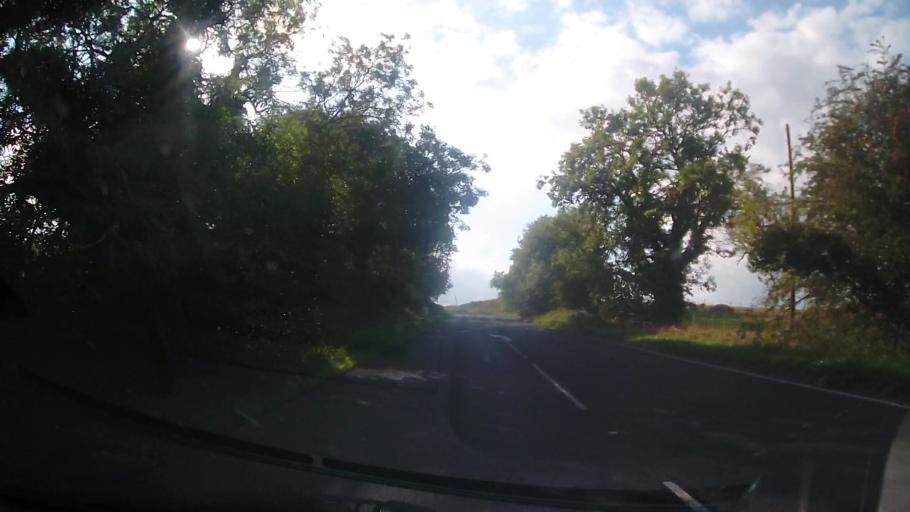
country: GB
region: England
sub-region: Kent
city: Hythe
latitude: 51.0941
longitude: 1.0912
